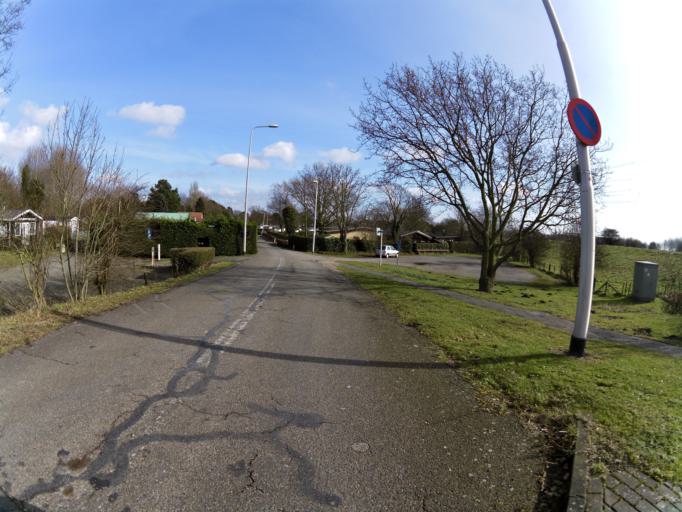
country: NL
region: South Holland
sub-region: Gemeente Brielle
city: Brielle
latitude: 51.9225
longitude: 4.1055
